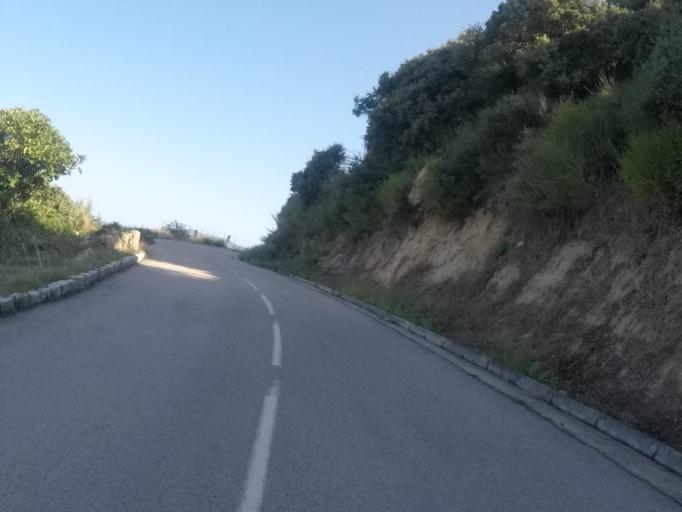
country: FR
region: Corsica
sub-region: Departement de la Corse-du-Sud
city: Olmeto
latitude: 41.7437
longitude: 8.8988
